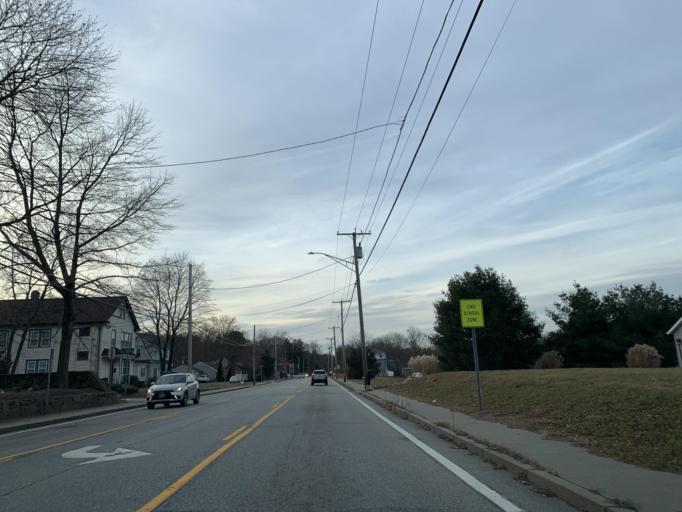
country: US
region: Rhode Island
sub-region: Providence County
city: Greenville
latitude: 41.8741
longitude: -71.5600
